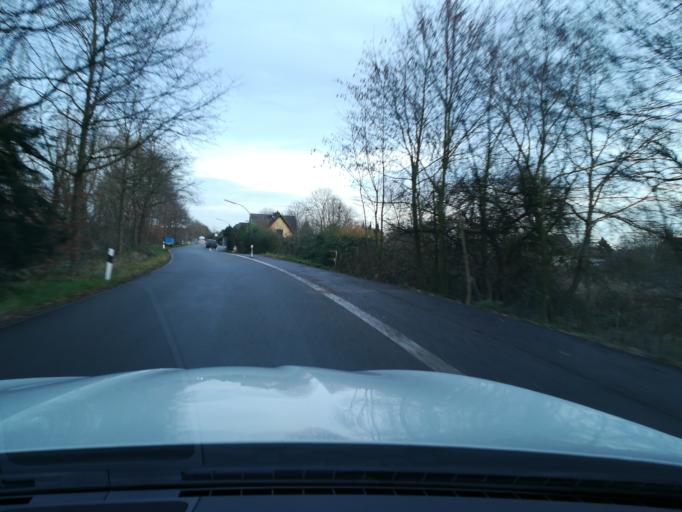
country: DE
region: Hamburg
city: Harburg
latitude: 53.4681
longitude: 10.0085
